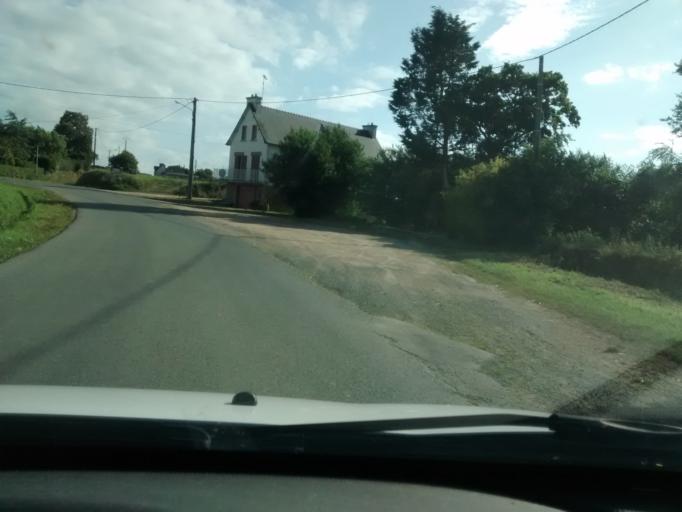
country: FR
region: Brittany
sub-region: Departement des Cotes-d'Armor
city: Penvenan
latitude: 48.8053
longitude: -3.2964
